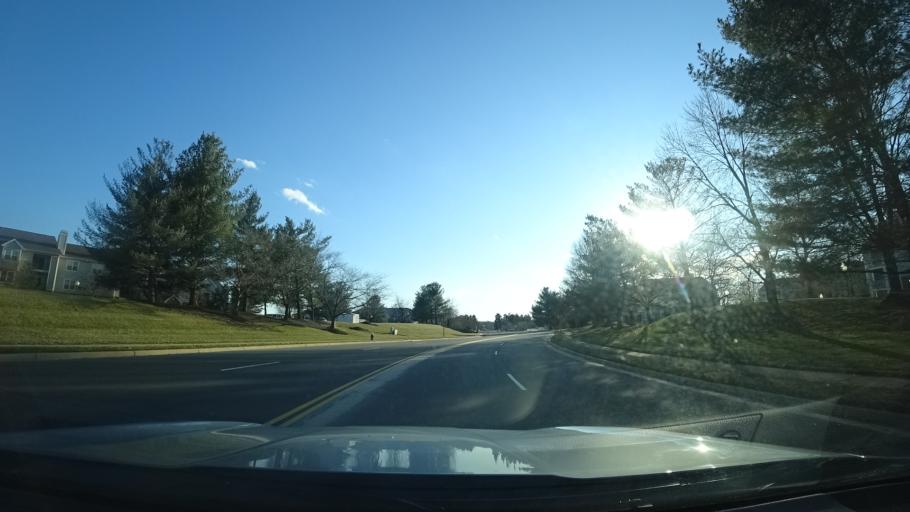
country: US
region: Virginia
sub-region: Loudoun County
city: University Center
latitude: 39.0538
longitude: -77.4378
